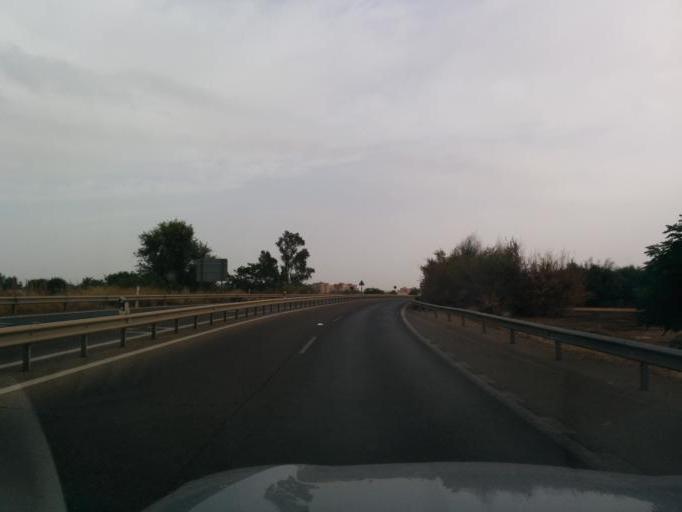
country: ES
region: Andalusia
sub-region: Provincia de Sevilla
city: Sevilla
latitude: 37.4328
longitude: -5.9657
